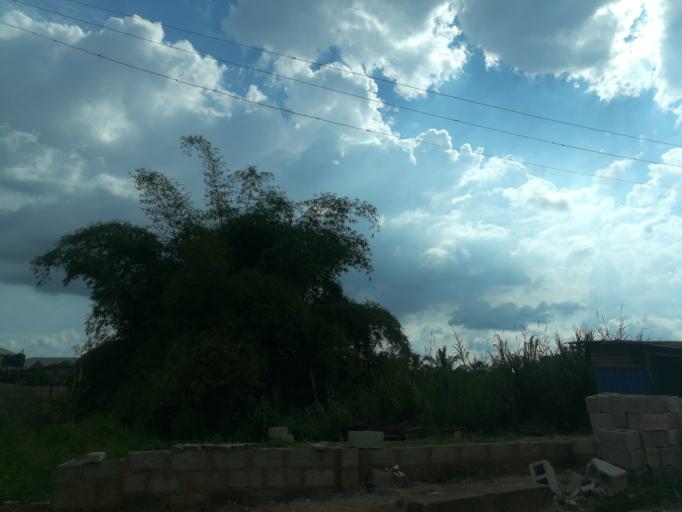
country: NG
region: Oyo
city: Ibadan
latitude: 7.4079
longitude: 3.8279
